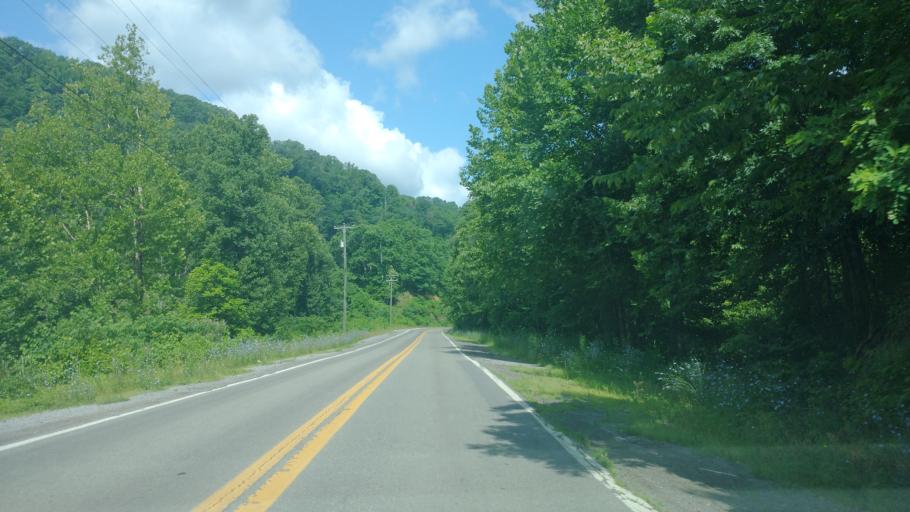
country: US
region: West Virginia
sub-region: McDowell County
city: Welch
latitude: 37.4099
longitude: -81.5360
